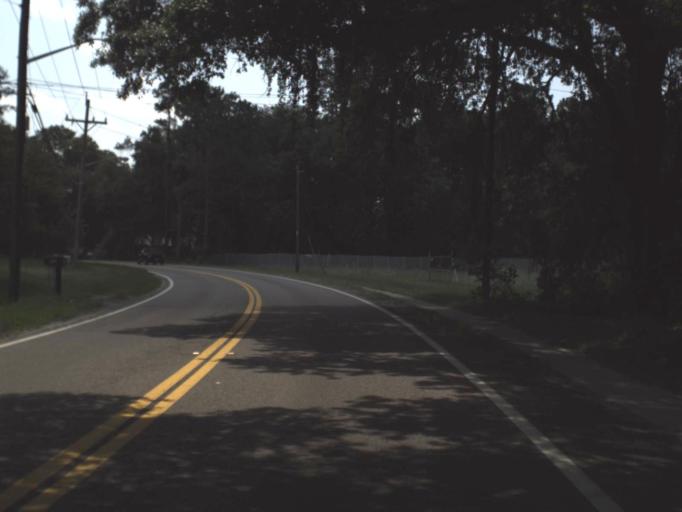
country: US
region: Florida
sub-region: Duval County
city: Jacksonville
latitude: 30.3668
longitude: -81.7437
